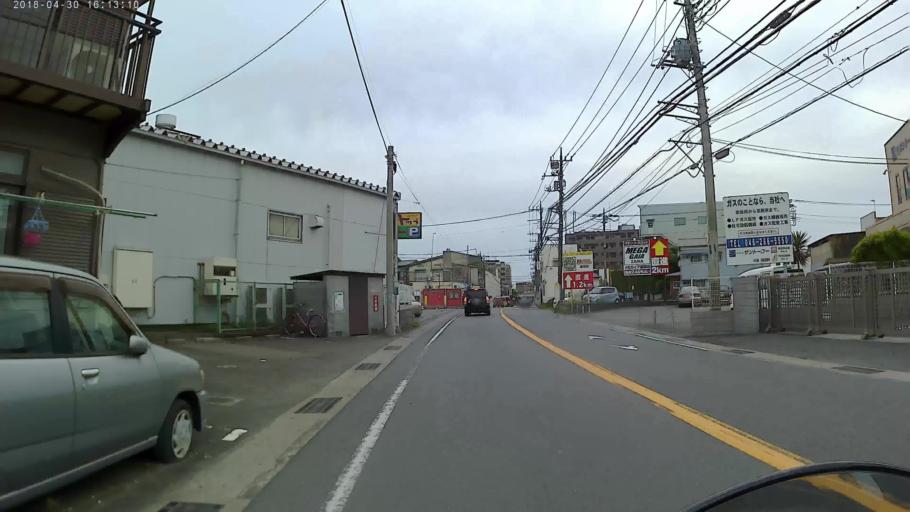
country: JP
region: Kanagawa
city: Minami-rinkan
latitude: 35.4913
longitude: 139.4313
